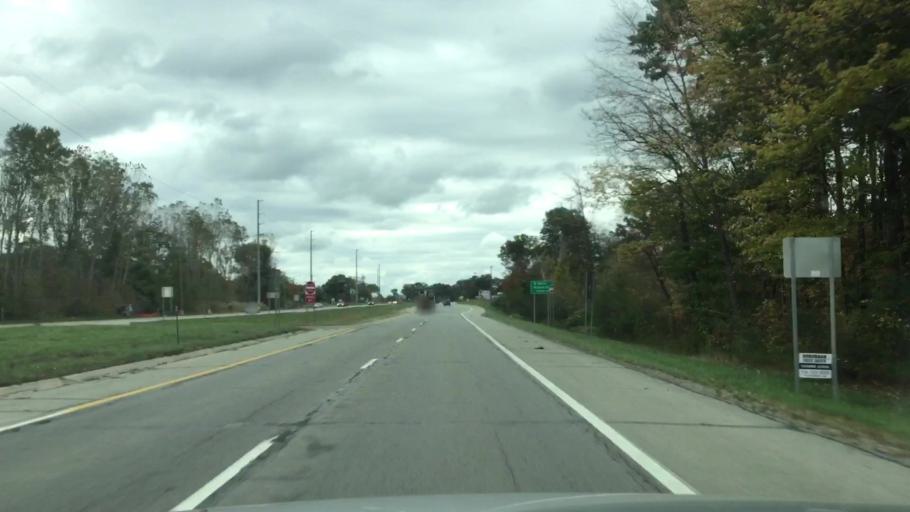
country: US
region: Michigan
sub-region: Livingston County
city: Brighton
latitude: 42.6357
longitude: -83.7174
